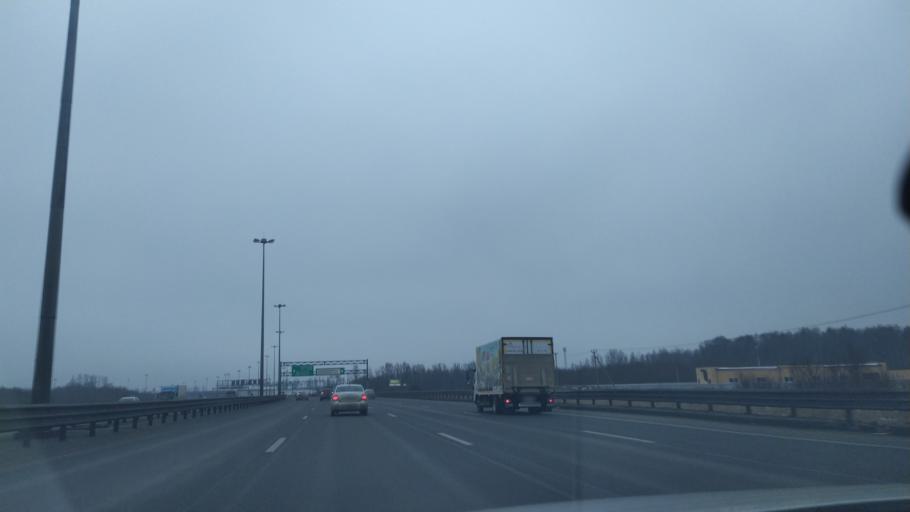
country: RU
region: St.-Petersburg
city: Krasnogvargeisky
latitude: 59.9966
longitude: 30.4775
